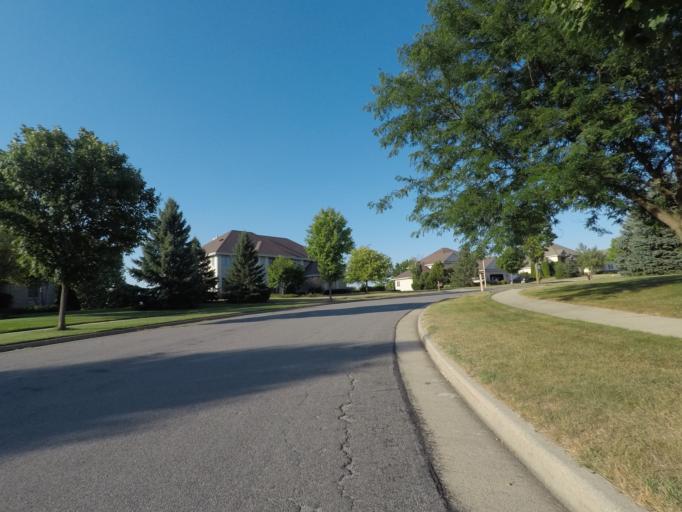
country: US
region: Wisconsin
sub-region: Dane County
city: Verona
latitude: 43.0064
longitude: -89.5377
